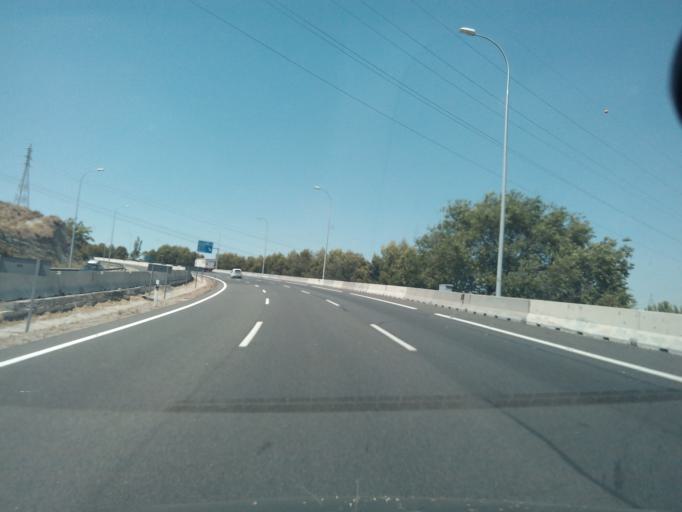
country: ES
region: Madrid
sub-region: Provincia de Madrid
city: Ciempozuelos
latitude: 40.0970
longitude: -3.6330
